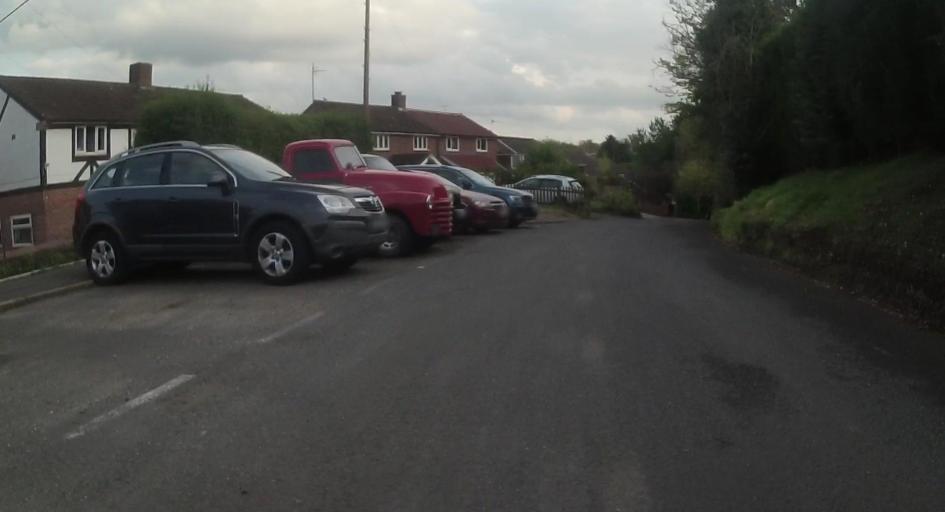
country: GB
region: England
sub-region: Hampshire
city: Tadley
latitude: 51.3987
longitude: -1.1799
